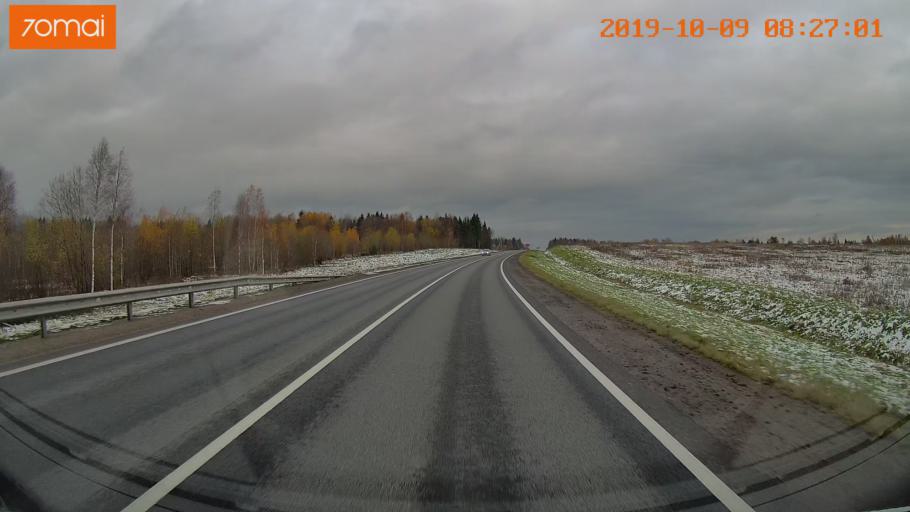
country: RU
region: Vologda
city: Gryazovets
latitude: 58.7988
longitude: 40.2560
